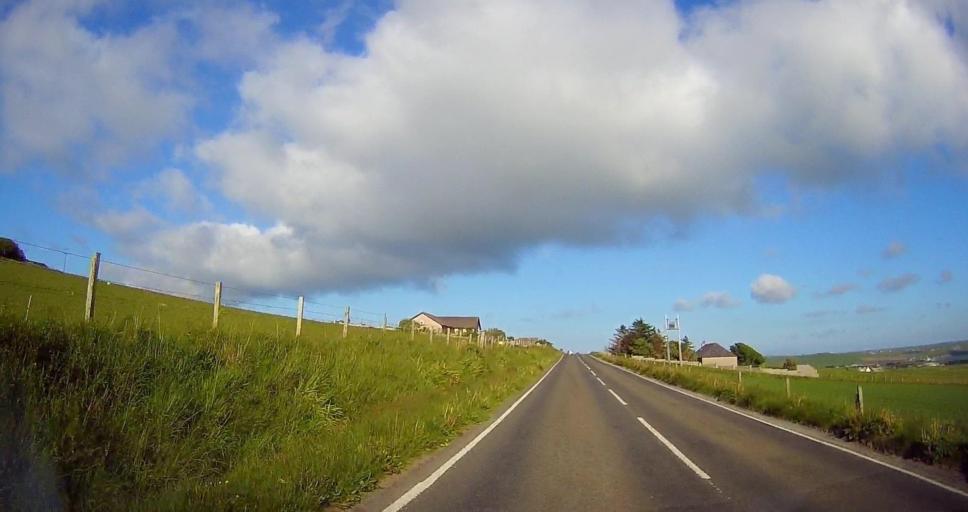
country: GB
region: Scotland
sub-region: Orkney Islands
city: Orkney
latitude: 58.9784
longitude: -3.0148
